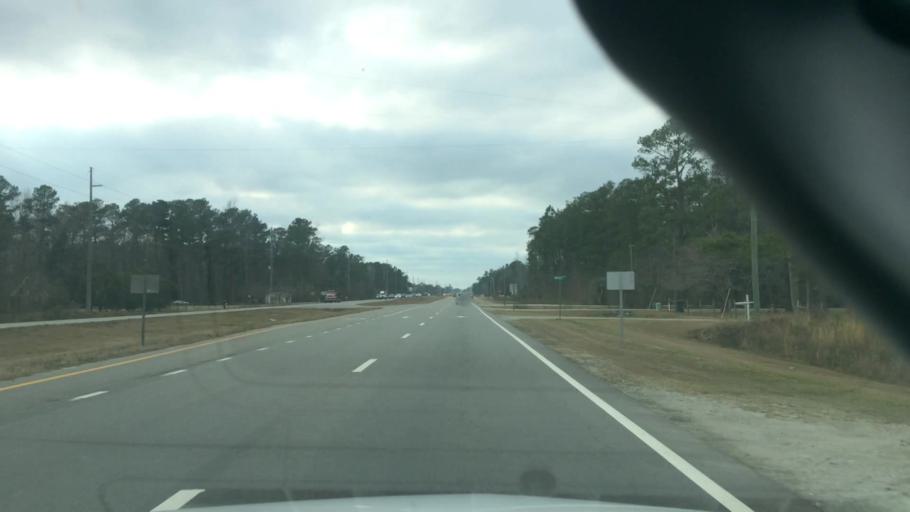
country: US
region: North Carolina
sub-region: Brunswick County
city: Calabash
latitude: 33.9419
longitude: -78.5331
